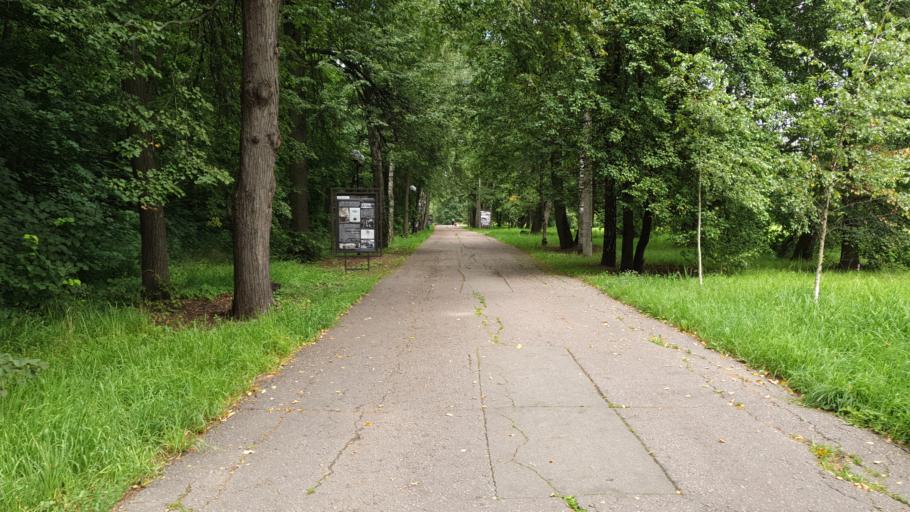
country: RU
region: Moskovskaya
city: Gorki-Leninskiye
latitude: 55.5109
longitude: 37.7709
